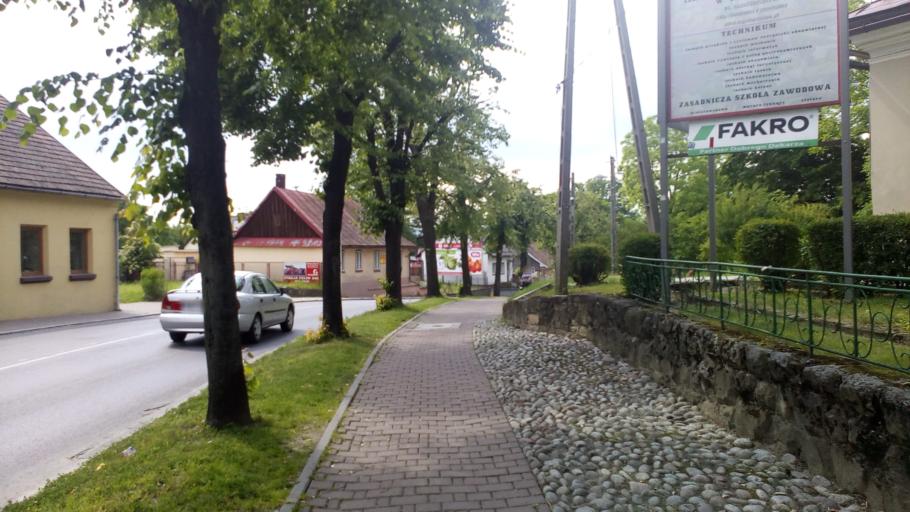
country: PL
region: Lesser Poland Voivodeship
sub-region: Powiat nowosadecki
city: Stary Sacz
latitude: 49.5657
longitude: 20.6313
